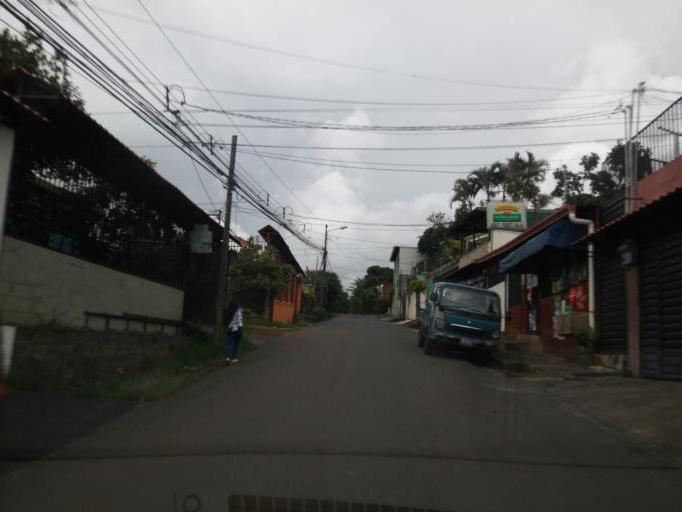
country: CR
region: Heredia
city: Mercedes
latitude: 10.0389
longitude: -84.1314
